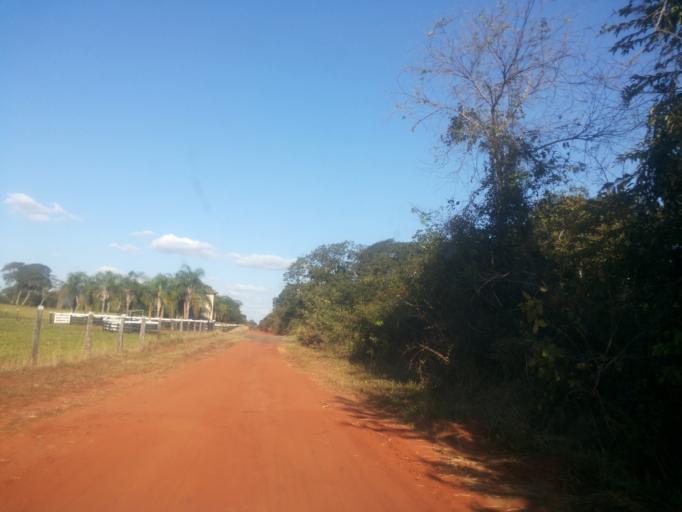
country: BR
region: Minas Gerais
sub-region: Santa Vitoria
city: Santa Vitoria
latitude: -19.0236
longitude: -50.4375
